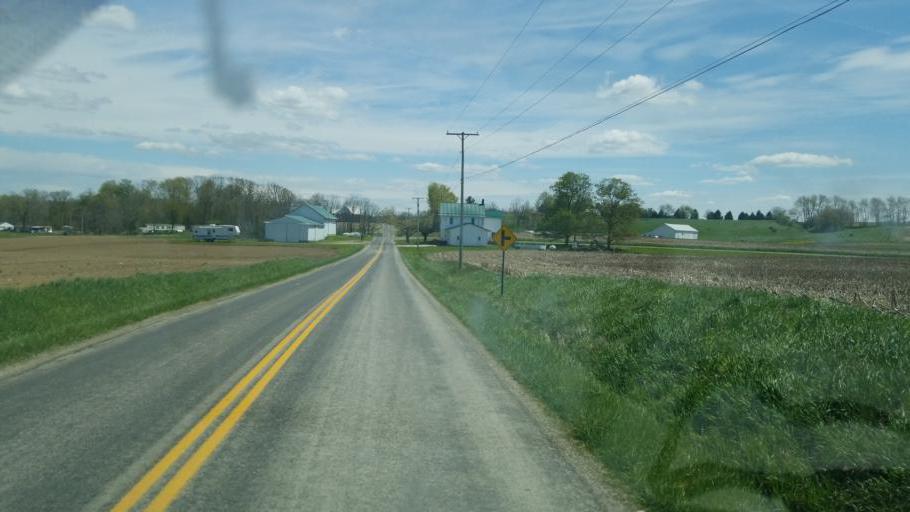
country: US
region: Ohio
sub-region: Ashland County
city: Loudonville
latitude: 40.7571
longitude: -82.1504
